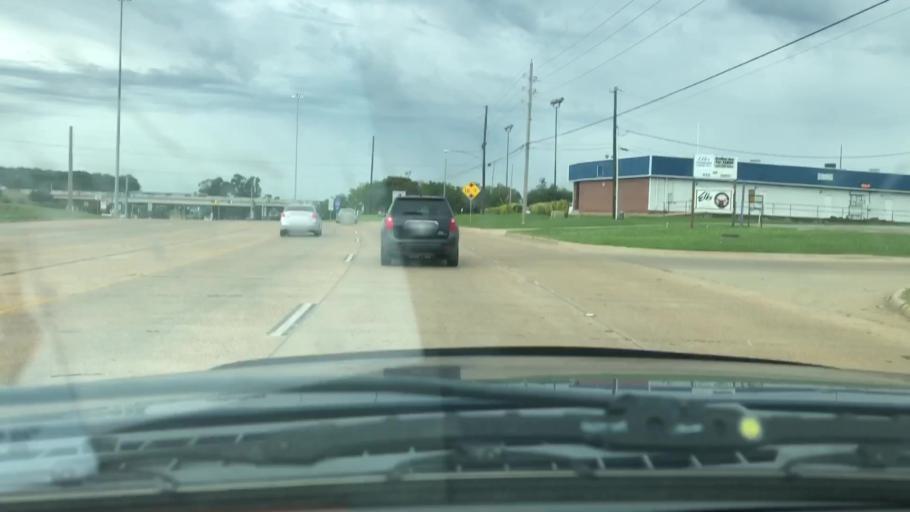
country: US
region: Texas
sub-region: Bowie County
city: Wake Village
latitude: 33.4432
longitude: -94.0940
